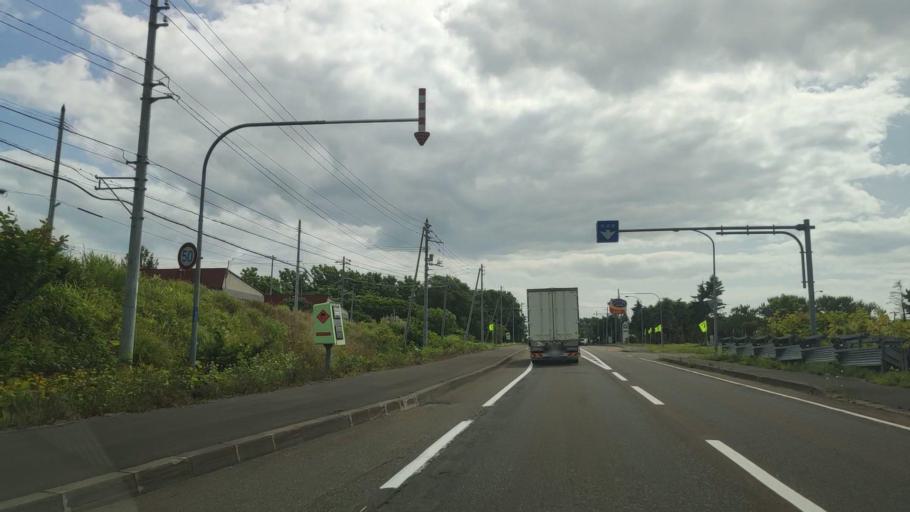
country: JP
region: Hokkaido
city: Rumoi
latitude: 44.5642
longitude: 141.7859
